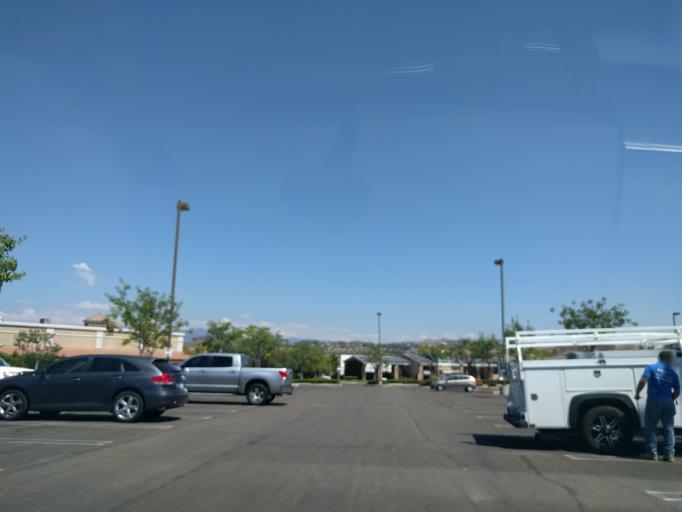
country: US
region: California
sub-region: Orange County
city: Ladera Ranch
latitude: 33.5574
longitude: -117.6597
